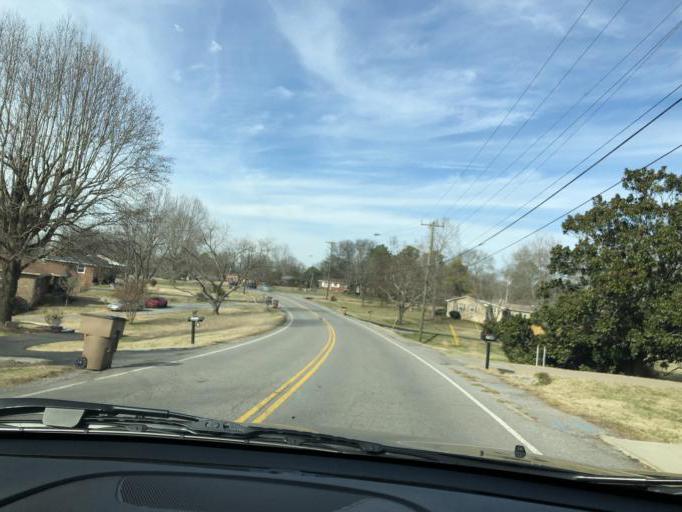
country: US
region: Tennessee
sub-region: Davidson County
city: Lakewood
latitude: 36.2076
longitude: -86.6806
